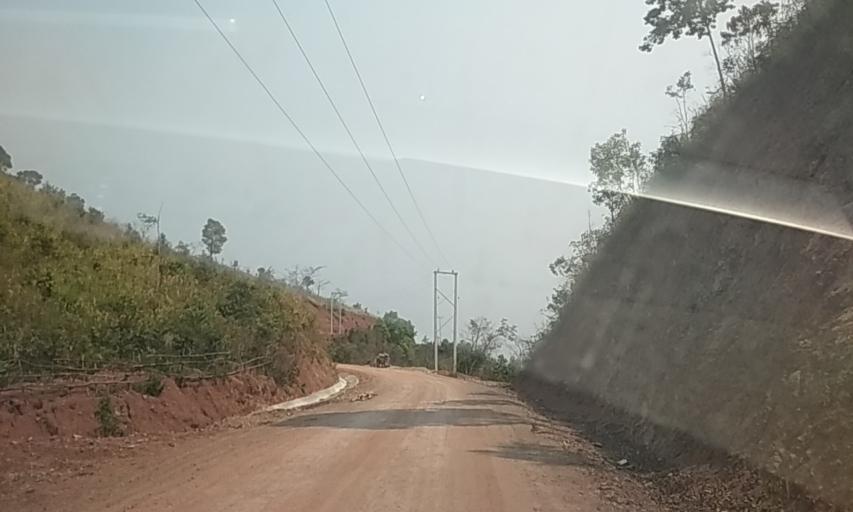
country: VN
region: Huyen Dien Bien
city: Dien Bien Phu
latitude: 21.4931
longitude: 102.7850
